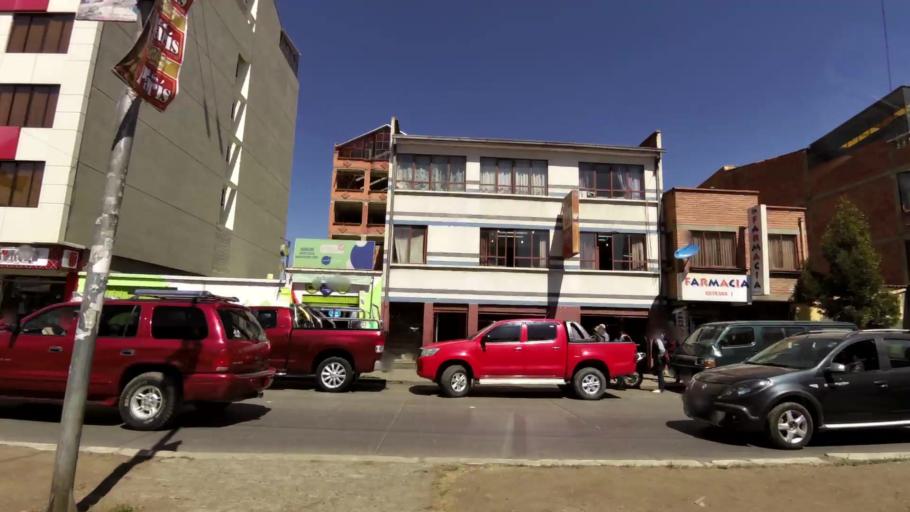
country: BO
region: La Paz
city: La Paz
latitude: -16.5233
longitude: -68.1527
